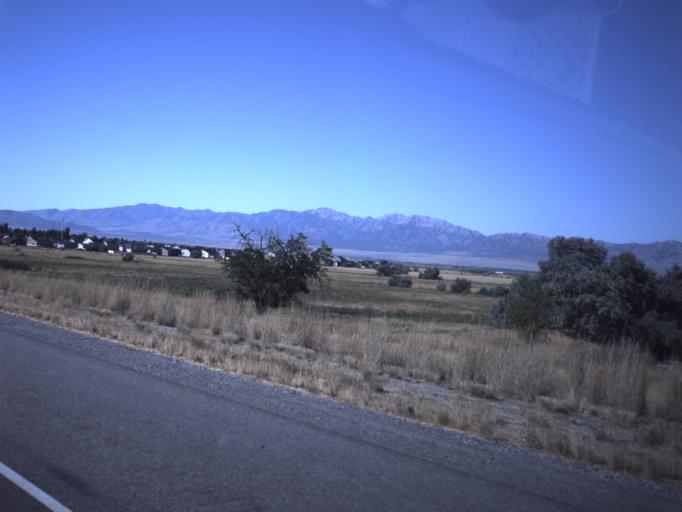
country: US
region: Utah
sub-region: Tooele County
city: Stansbury park
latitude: 40.6602
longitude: -112.2895
